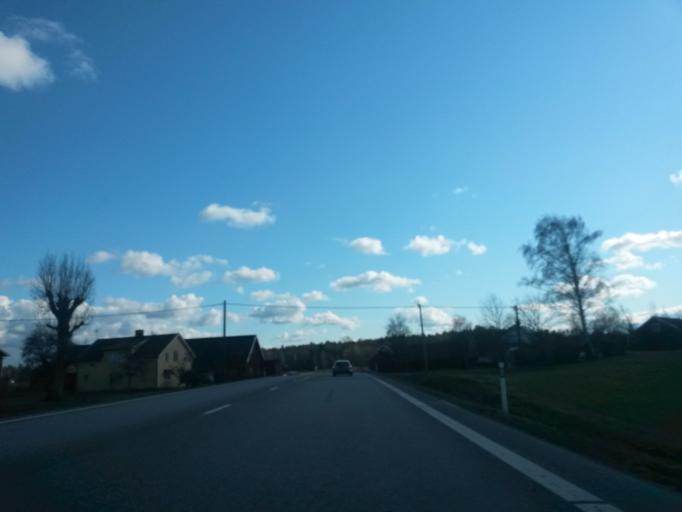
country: SE
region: Vaestra Goetaland
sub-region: Vargarda Kommun
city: Vargarda
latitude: 58.0755
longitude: 12.8148
